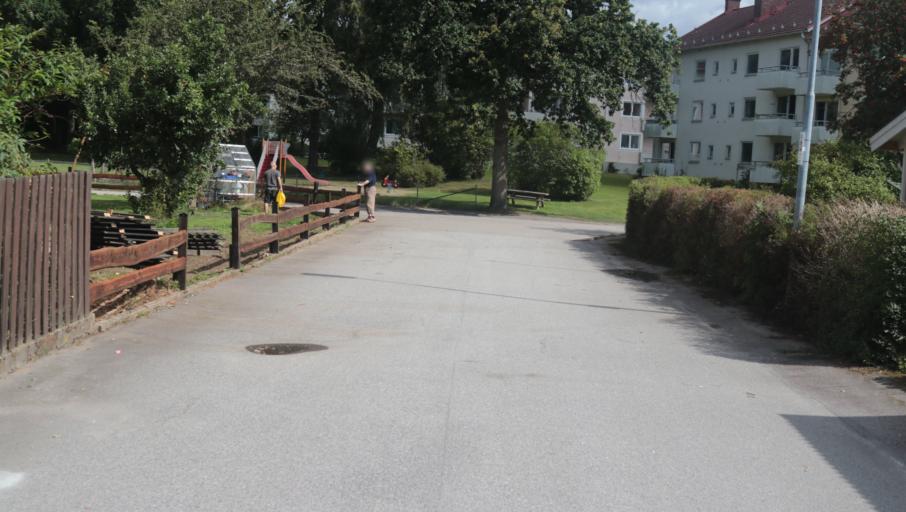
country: SE
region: Blekinge
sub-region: Karlshamns Kommun
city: Svangsta
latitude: 56.2614
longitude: 14.7635
